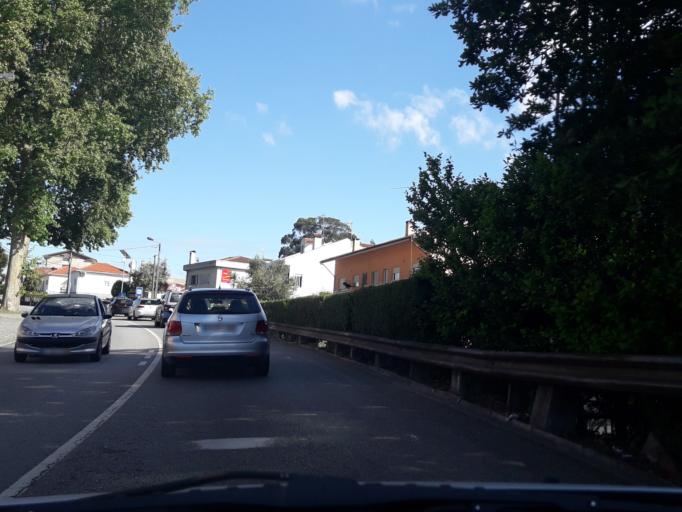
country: PT
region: Braga
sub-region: Vila Nova de Famalicao
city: Vila Nova de Famalicao
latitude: 41.3965
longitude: -8.5152
